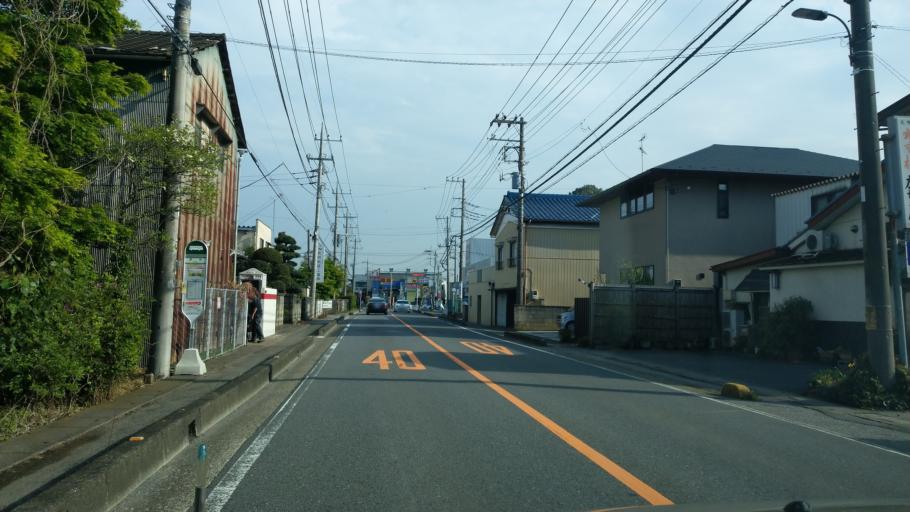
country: JP
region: Saitama
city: Iwatsuki
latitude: 35.9332
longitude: 139.7116
